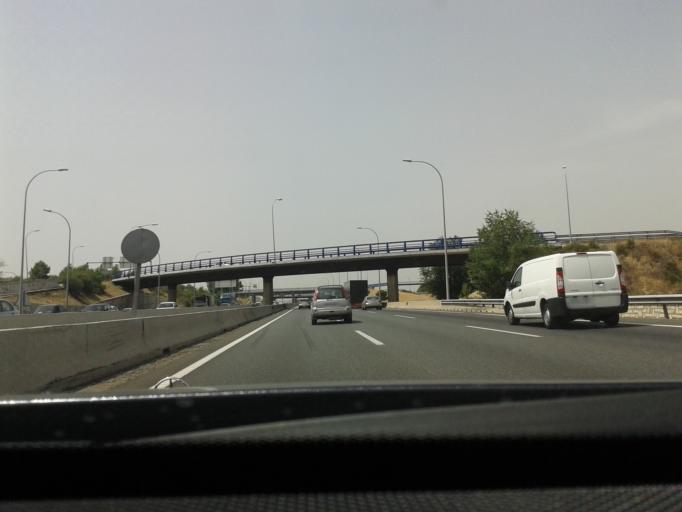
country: ES
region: Madrid
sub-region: Provincia de Madrid
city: Torrejon de Ardoz
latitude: 40.4654
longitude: -3.4807
